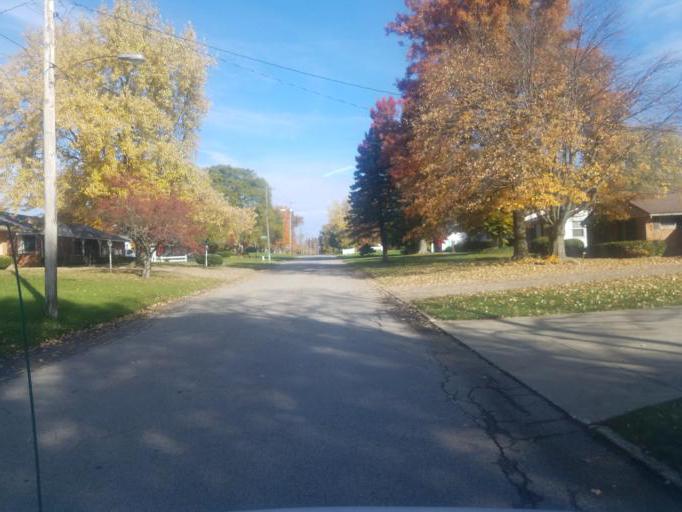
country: US
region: Ohio
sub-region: Richland County
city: Mansfield
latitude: 40.7289
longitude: -82.5242
